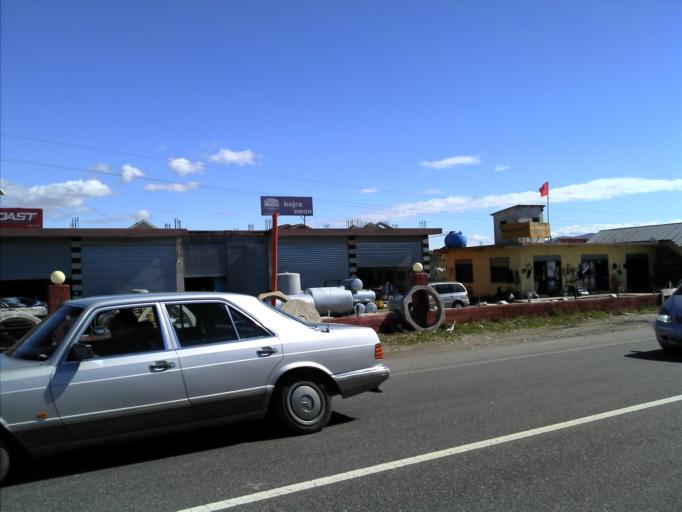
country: AL
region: Shkoder
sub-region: Rrethi i Shkodres
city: Shkoder
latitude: 42.0987
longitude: 19.5057
